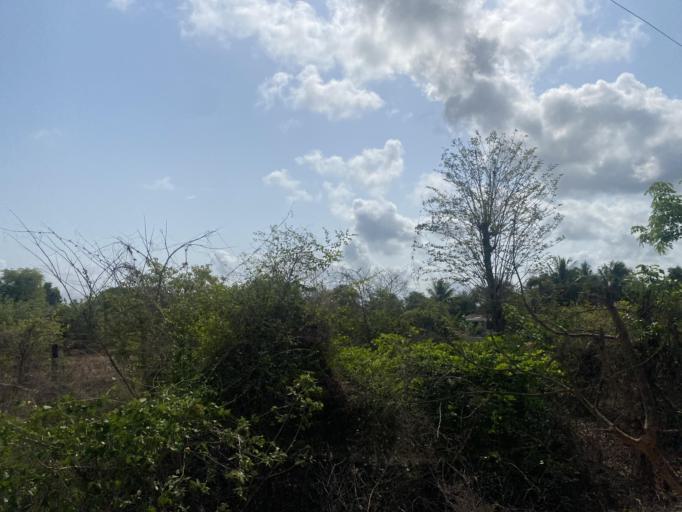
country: IN
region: Daman and Diu
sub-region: Daman District
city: Daman
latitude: 20.3334
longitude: 72.8076
